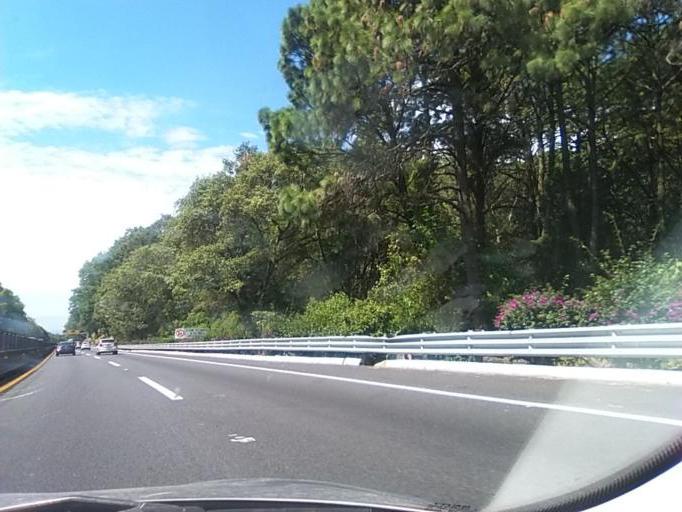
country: MX
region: Morelos
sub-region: Cuernavaca
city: Villa Santiago
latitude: 18.9891
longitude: -99.2068
